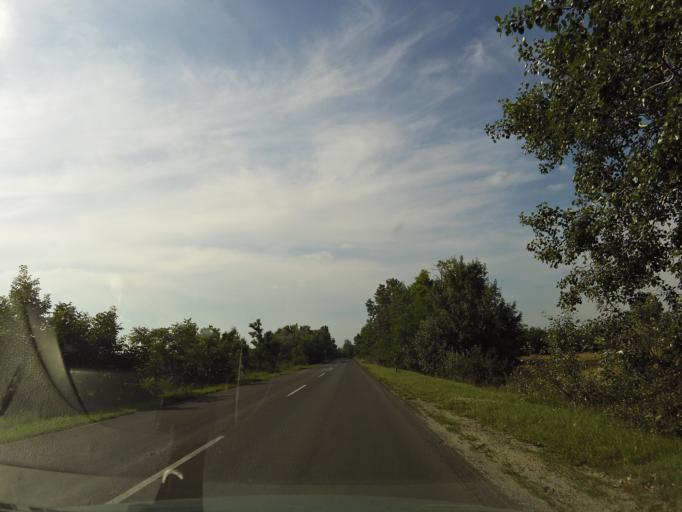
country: HU
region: Csongrad
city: Szatymaz
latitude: 46.3703
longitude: 20.0438
